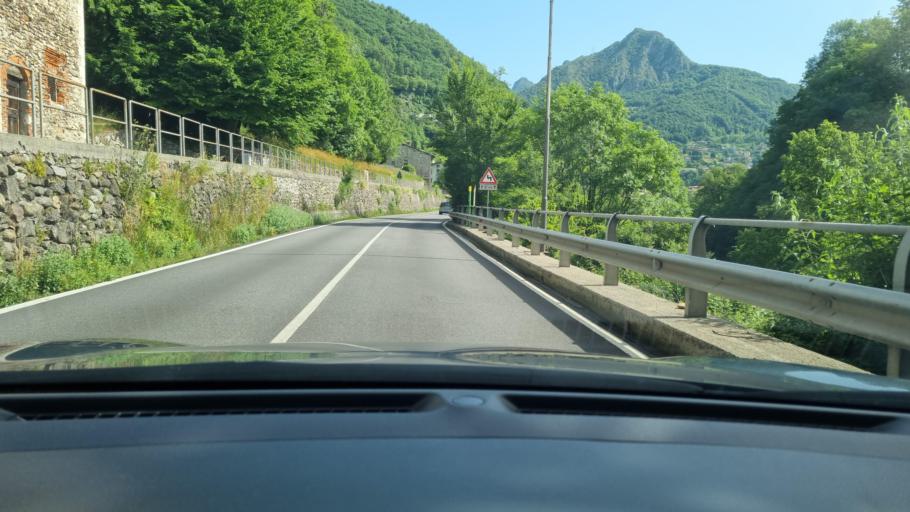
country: IT
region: Lombardy
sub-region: Provincia di Bergamo
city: Zogno
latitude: 45.8008
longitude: 9.6697
